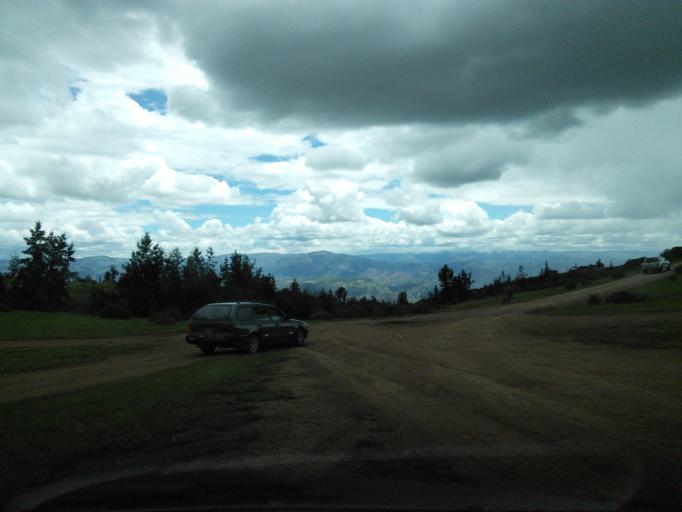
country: PE
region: Ayacucho
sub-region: Provincia de Huamanga
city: Quinua
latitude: -13.0430
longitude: -74.1290
